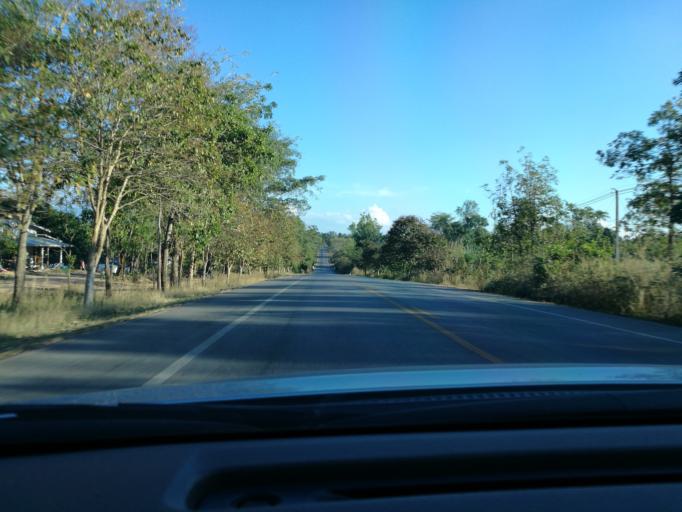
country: TH
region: Phitsanulok
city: Nakhon Thai
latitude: 17.0398
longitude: 100.8138
